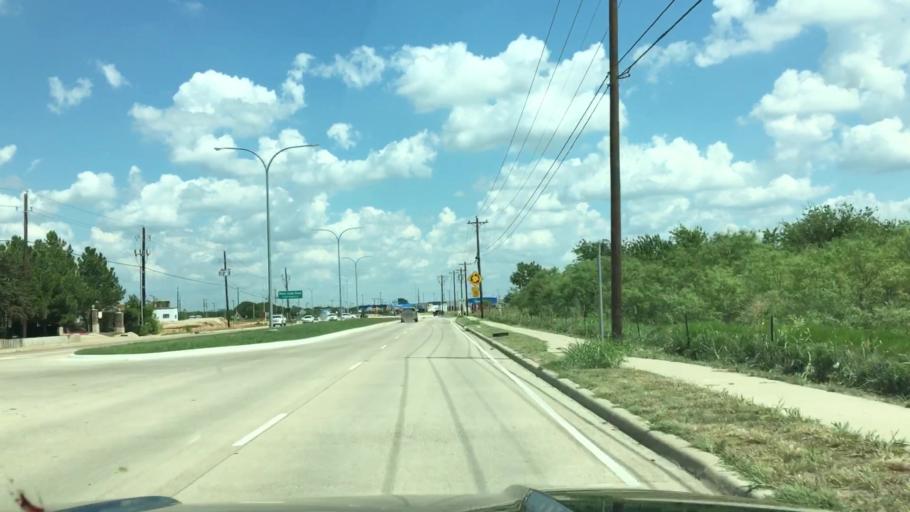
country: US
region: Texas
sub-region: Tarrant County
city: Keller
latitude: 32.9313
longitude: -97.2752
